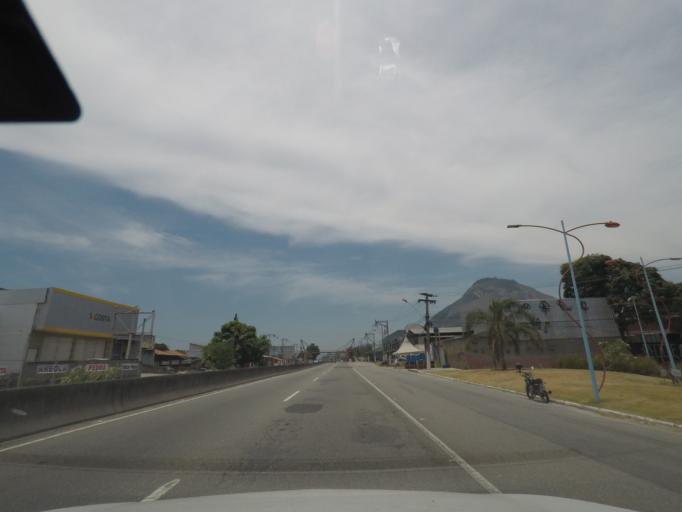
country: BR
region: Rio de Janeiro
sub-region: Marica
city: Marica
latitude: -22.9325
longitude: -42.8886
